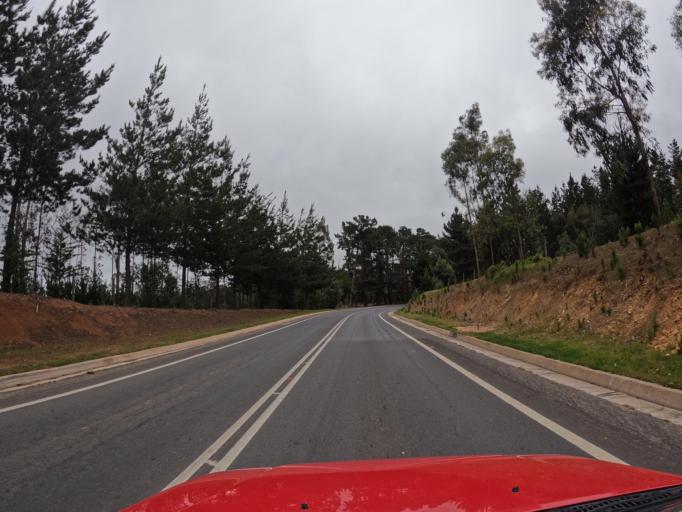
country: CL
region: O'Higgins
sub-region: Provincia de Colchagua
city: Santa Cruz
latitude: -34.5787
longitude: -72.0156
